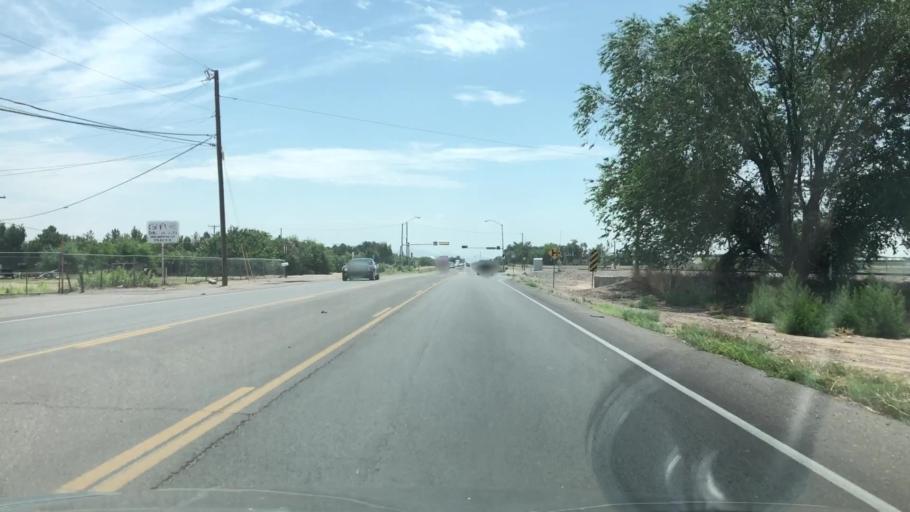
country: US
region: New Mexico
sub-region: Dona Ana County
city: University Park
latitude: 32.2630
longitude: -106.7588
